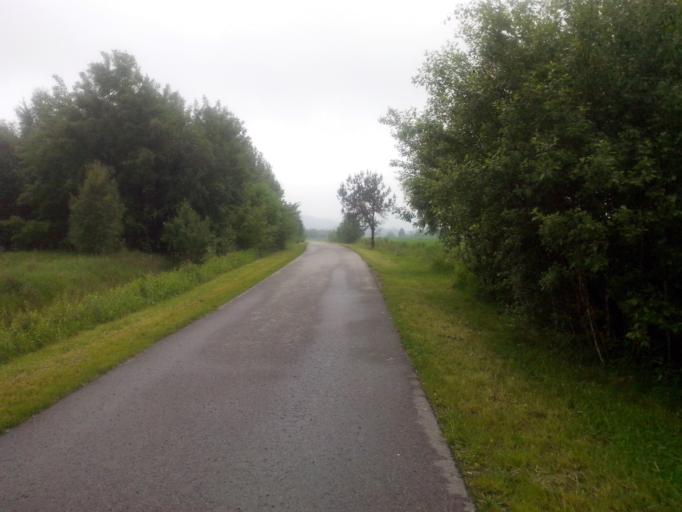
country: PL
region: Subcarpathian Voivodeship
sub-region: Powiat strzyzowski
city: Wysoka Strzyzowska
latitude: 49.8118
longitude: 21.7836
